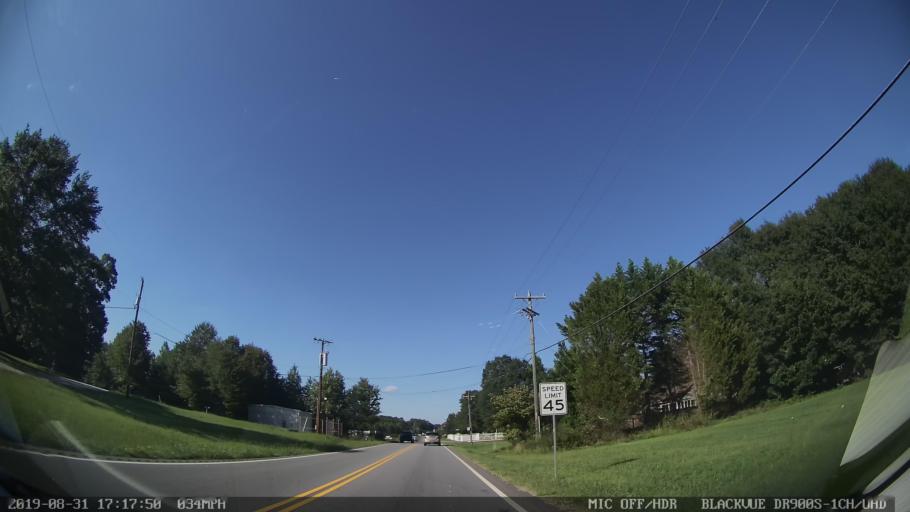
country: US
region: South Carolina
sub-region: Spartanburg County
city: Valley Falls
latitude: 35.0342
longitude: -81.9476
